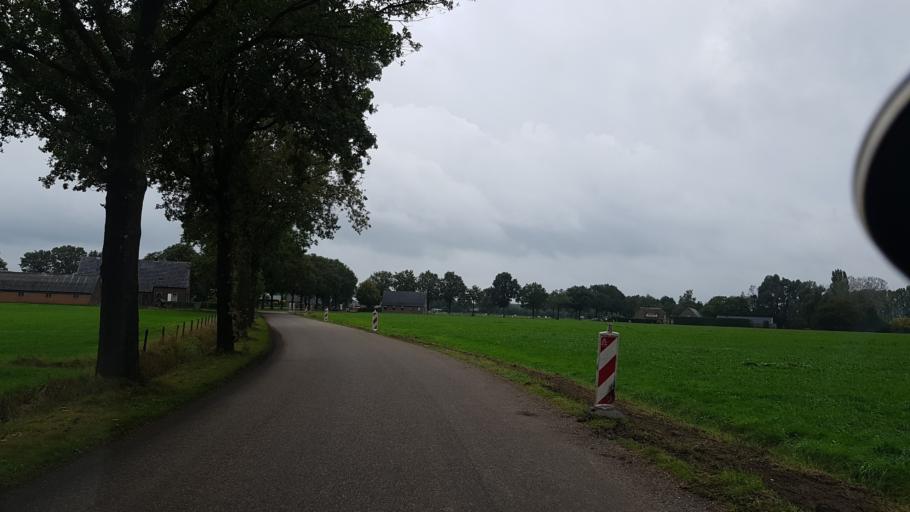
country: NL
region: Gelderland
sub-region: Gemeente Apeldoorn
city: Apeldoorn
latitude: 52.1902
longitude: 6.0305
